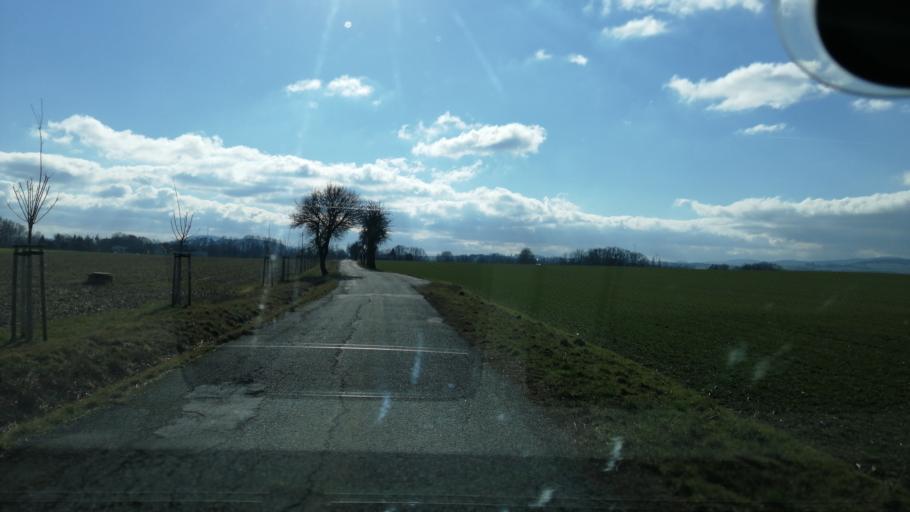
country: DE
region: Saxony
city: Weissenberg
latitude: 51.1737
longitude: 14.7119
